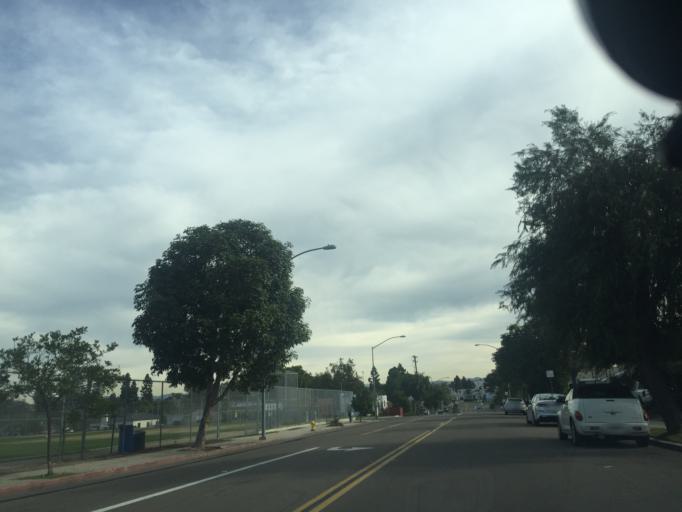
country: US
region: California
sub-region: San Diego County
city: San Diego
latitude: 32.7571
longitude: -117.1039
